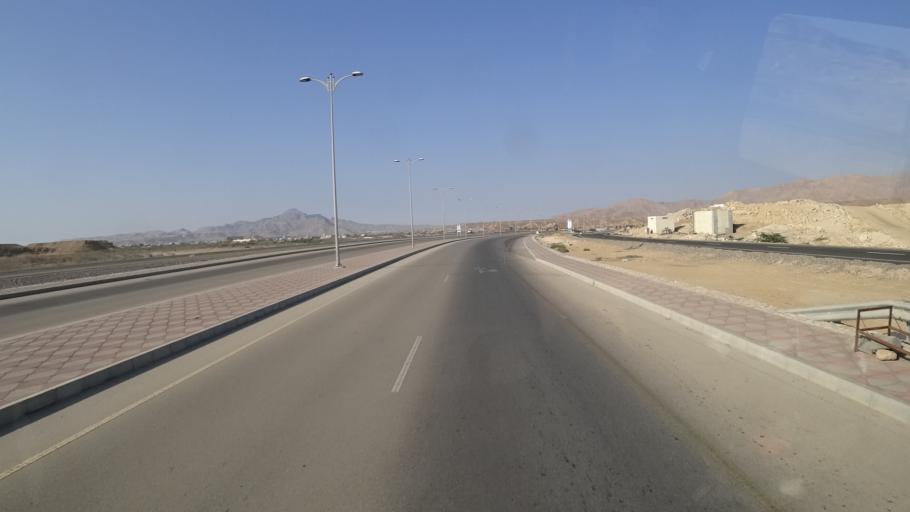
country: OM
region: Ash Sharqiyah
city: Sur
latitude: 22.5845
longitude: 59.4747
